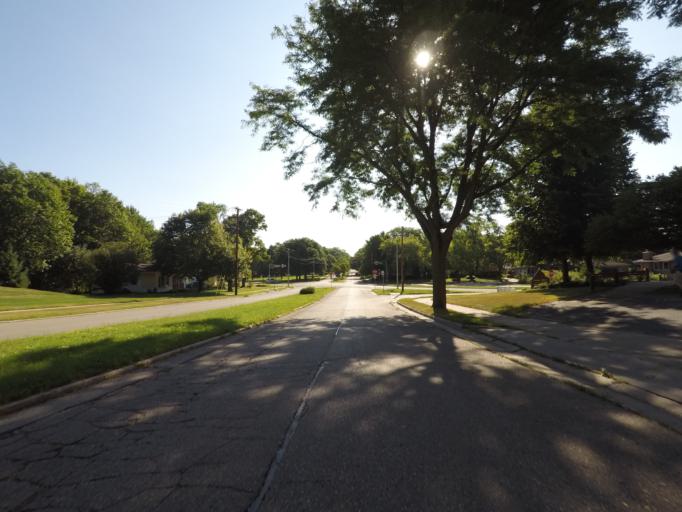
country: US
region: Wisconsin
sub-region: Dane County
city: Shorewood Hills
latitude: 43.0536
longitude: -89.4667
